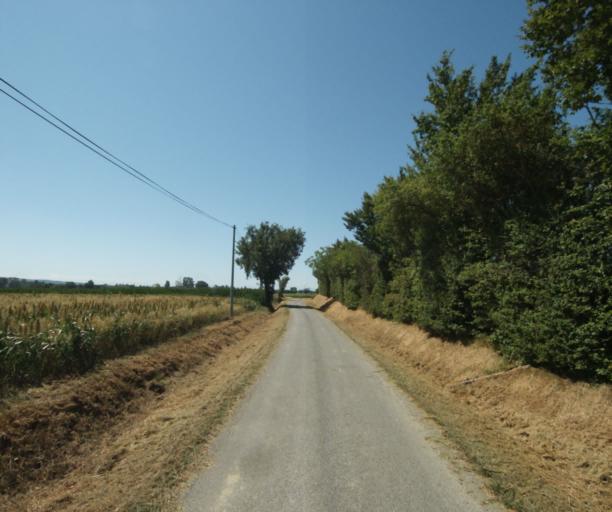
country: FR
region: Midi-Pyrenees
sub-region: Departement de la Haute-Garonne
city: Revel
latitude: 43.4992
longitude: 1.9567
